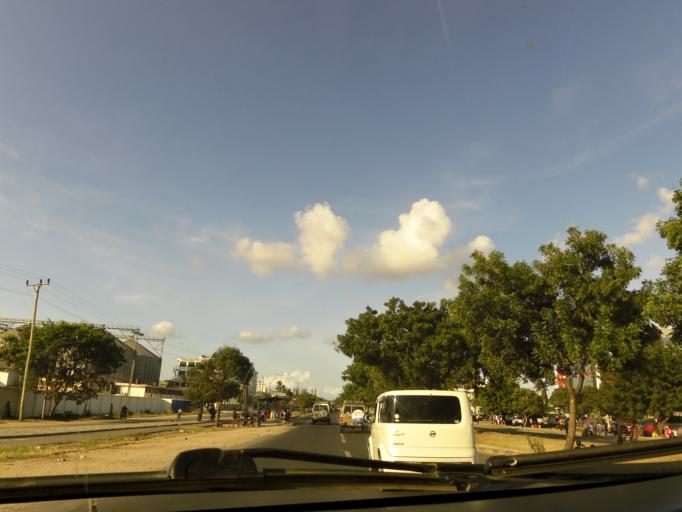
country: TZ
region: Dar es Salaam
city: Dar es Salaam
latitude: -6.8391
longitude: 39.2557
